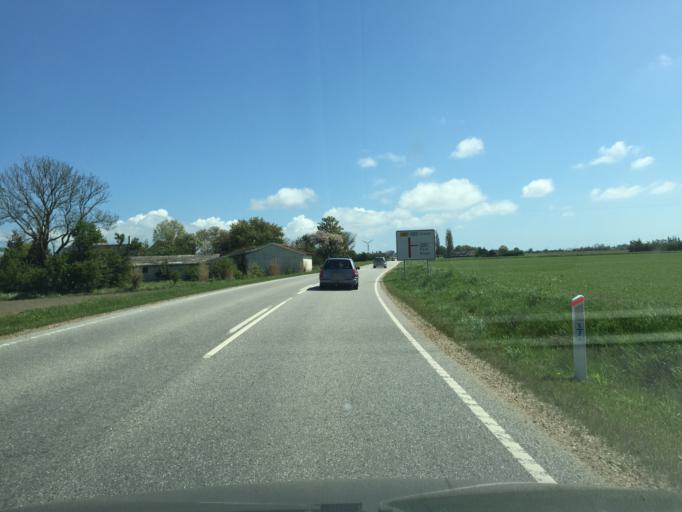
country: DK
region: Zealand
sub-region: Vordingborg Kommune
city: Stege
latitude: 54.9681
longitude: 12.2160
